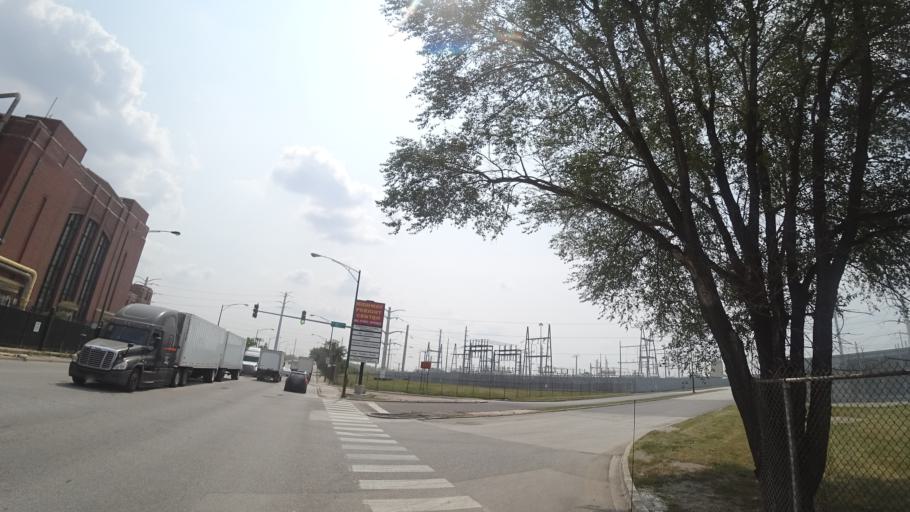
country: US
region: Illinois
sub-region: Cook County
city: Cicero
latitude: 41.8290
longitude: -87.7243
